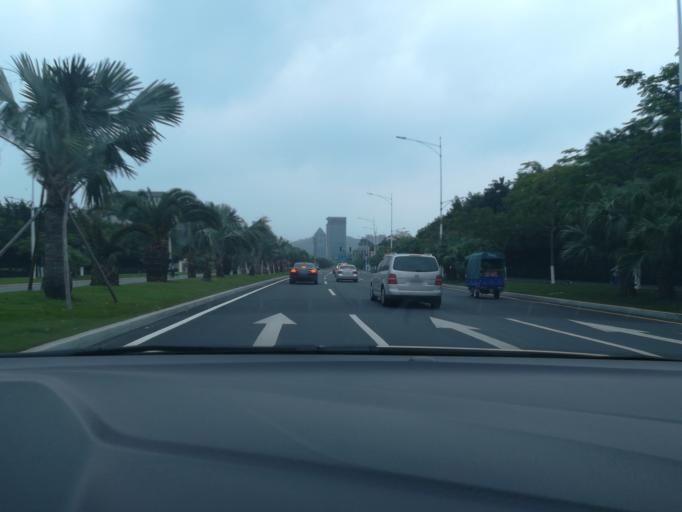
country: CN
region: Guangdong
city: Nansha
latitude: 22.7805
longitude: 113.5945
